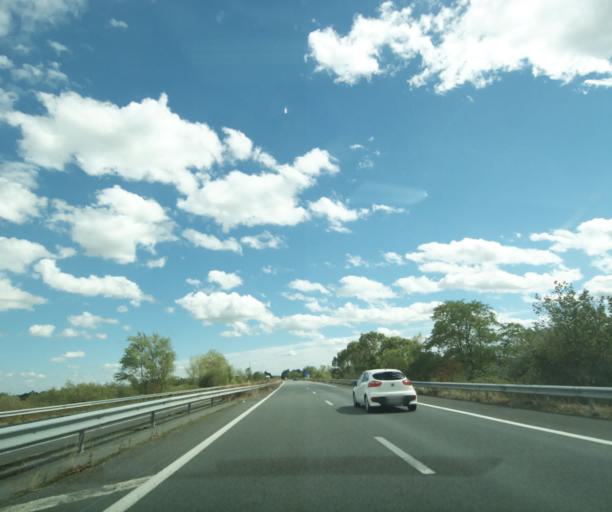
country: FR
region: Aquitaine
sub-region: Departement du Lot-et-Garonne
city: Meilhan-sur-Garonne
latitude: 44.4777
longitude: 0.0267
